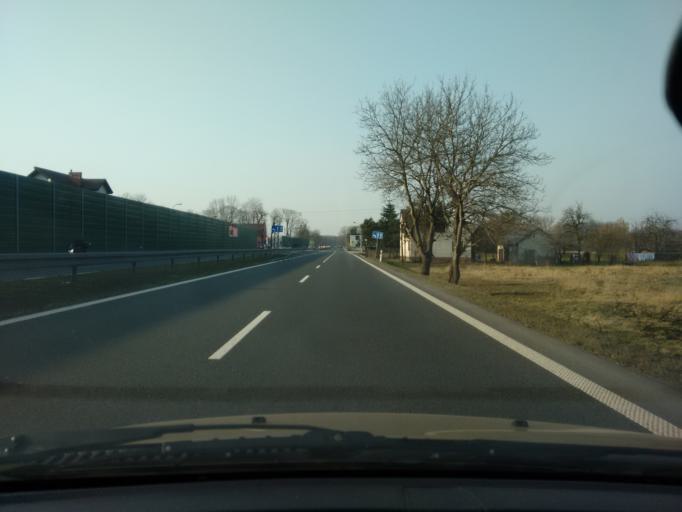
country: PL
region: Silesian Voivodeship
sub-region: Powiat cieszynski
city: Ochaby
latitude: 49.8508
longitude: 18.7615
